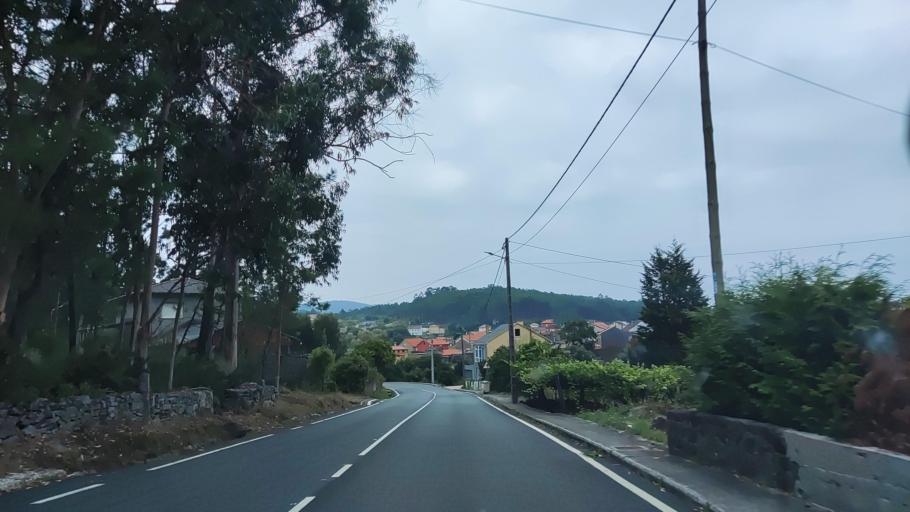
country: ES
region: Galicia
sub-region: Provincia de Pontevedra
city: Catoira
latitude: 42.6646
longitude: -8.7448
